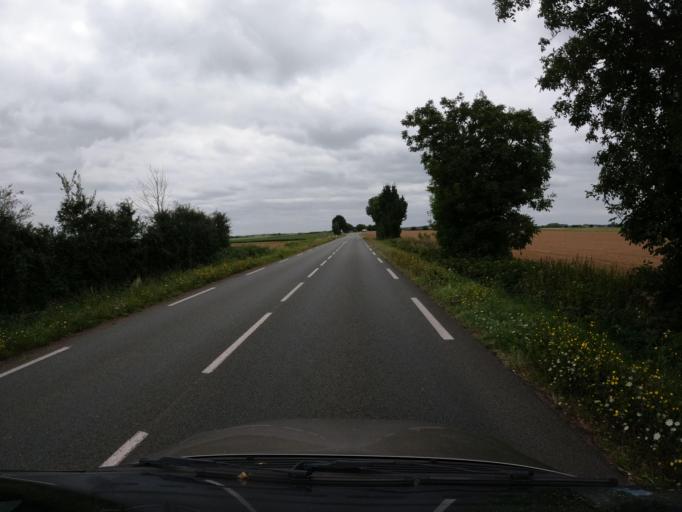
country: FR
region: Pays de la Loire
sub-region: Departement de la Vendee
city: Sainte-Hermine
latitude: 46.5460
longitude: -1.0344
